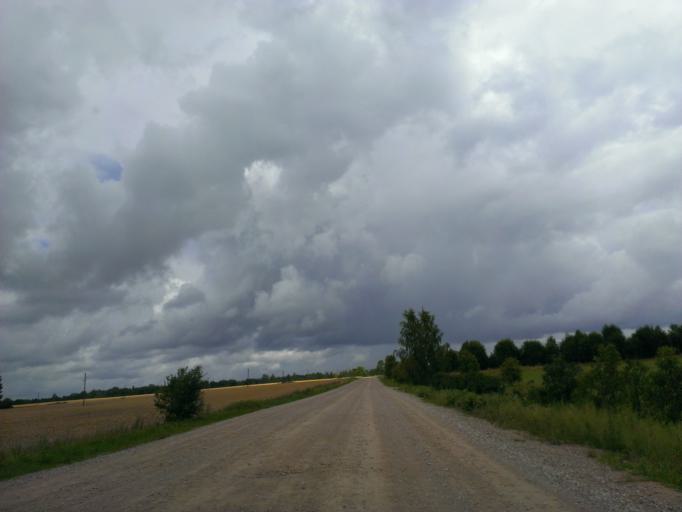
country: LV
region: Sigulda
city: Sigulda
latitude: 57.1895
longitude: 24.9408
